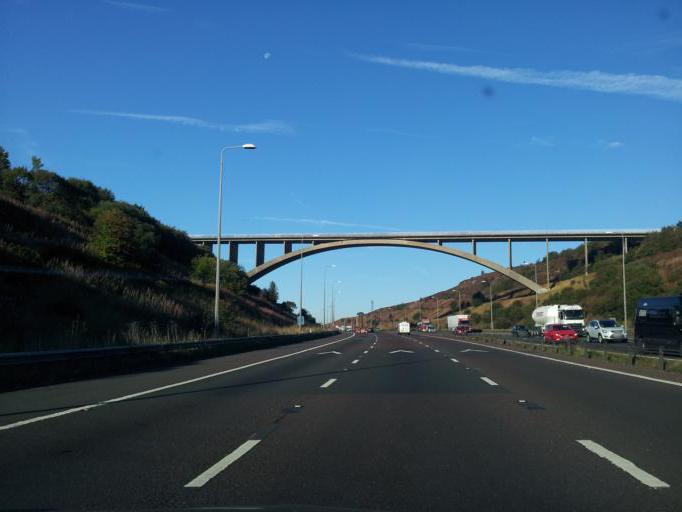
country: GB
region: England
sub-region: Calderdale
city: Ripponden
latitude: 53.6475
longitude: -1.9278
